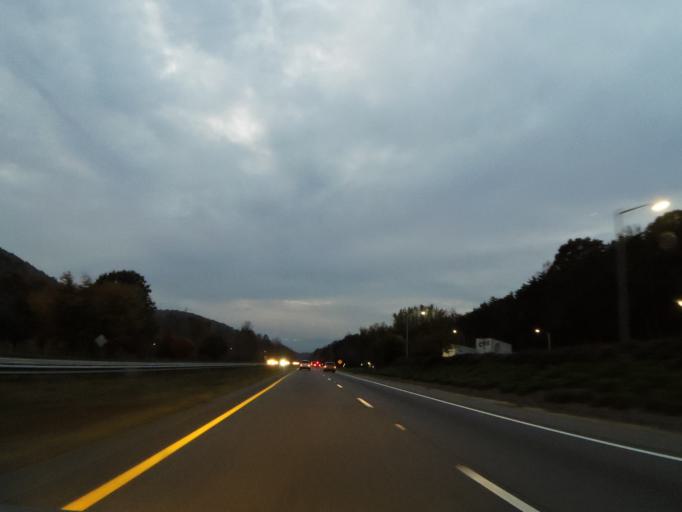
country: US
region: North Carolina
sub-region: McDowell County
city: West Marion
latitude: 35.6398
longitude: -82.0181
